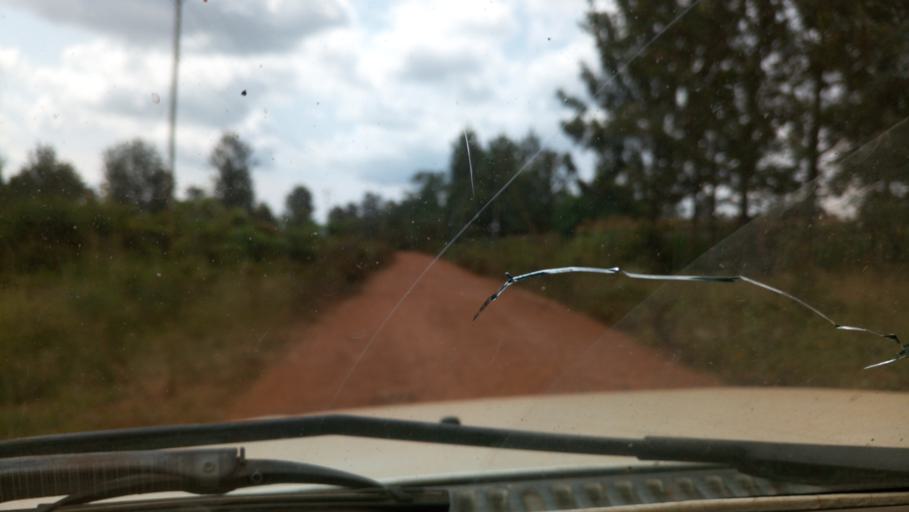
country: KE
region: Murang'a District
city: Karuri
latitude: -0.7424
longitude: 37.1994
